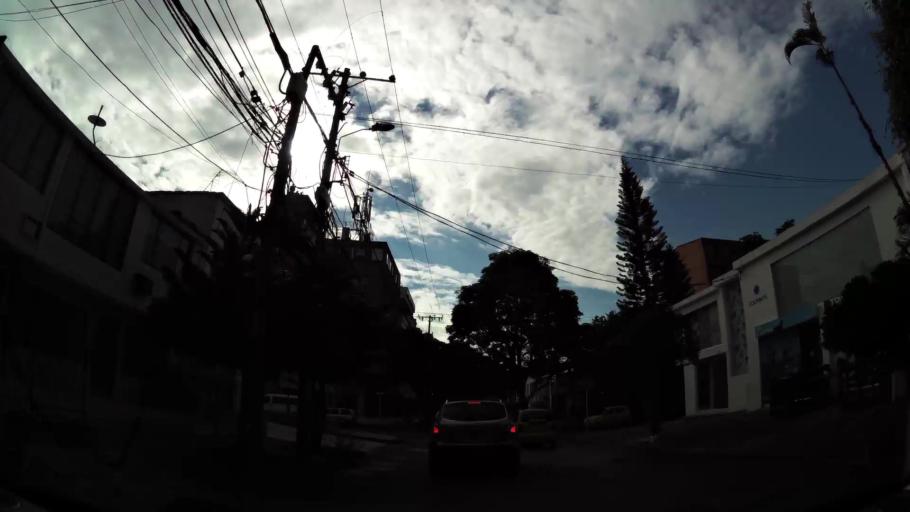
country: CO
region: Valle del Cauca
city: Cali
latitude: 3.4693
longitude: -76.5296
